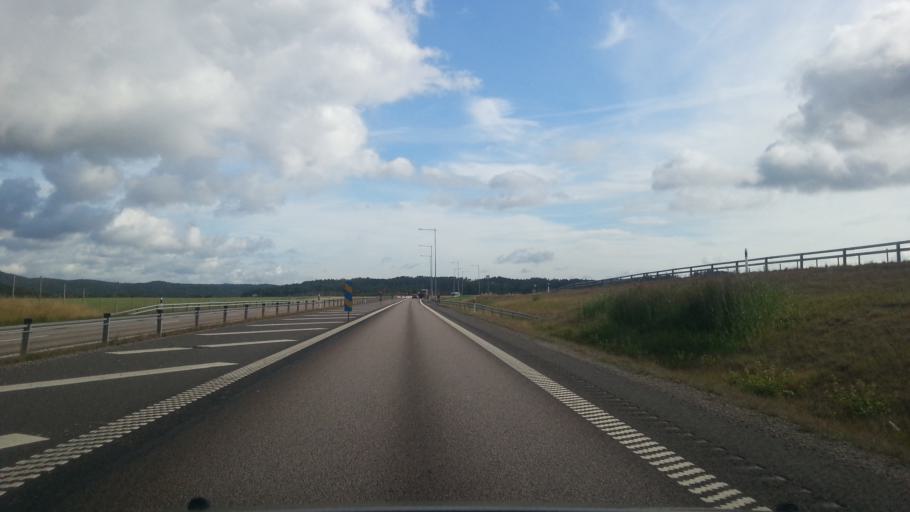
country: SE
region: Vaestra Goetaland
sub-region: Lilla Edets Kommun
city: Lilla Edet
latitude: 58.1962
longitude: 12.1498
